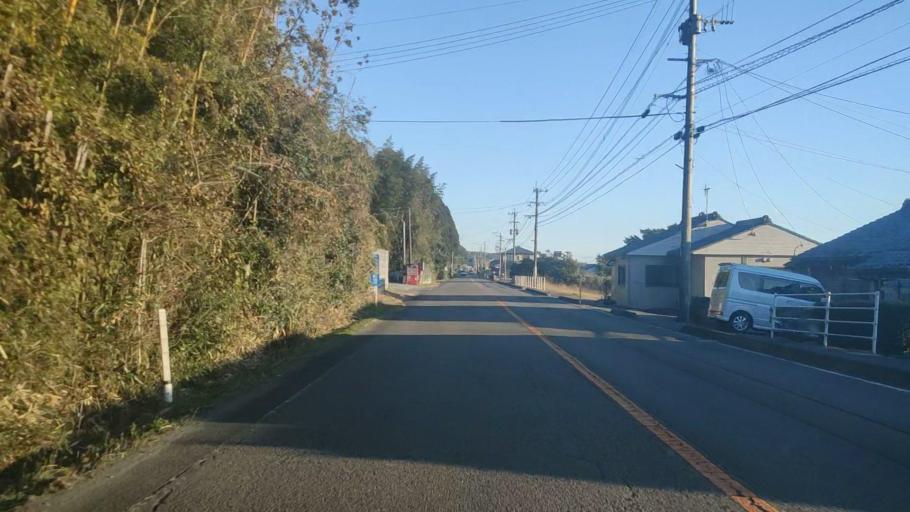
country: JP
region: Miyazaki
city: Takanabe
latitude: 32.0798
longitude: 131.5087
